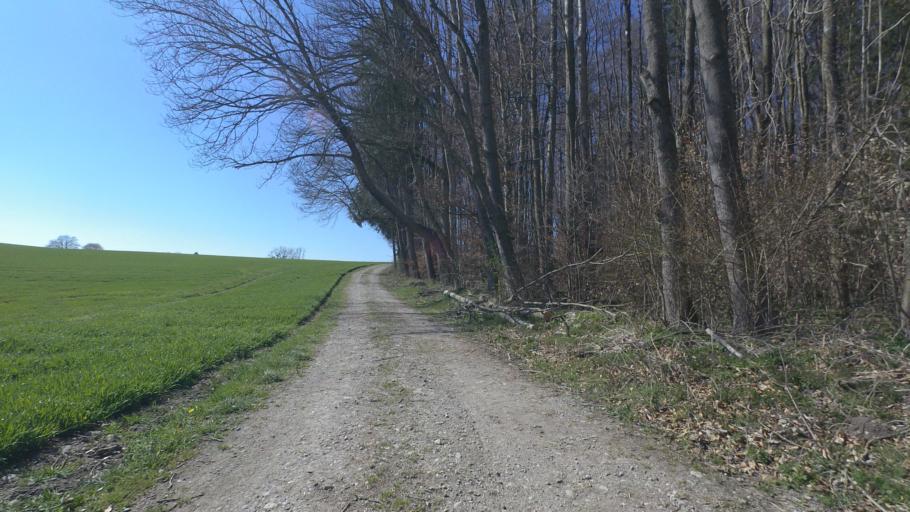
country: DE
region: Bavaria
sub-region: Upper Bavaria
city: Seeon-Seebruck
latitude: 47.9434
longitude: 12.4989
